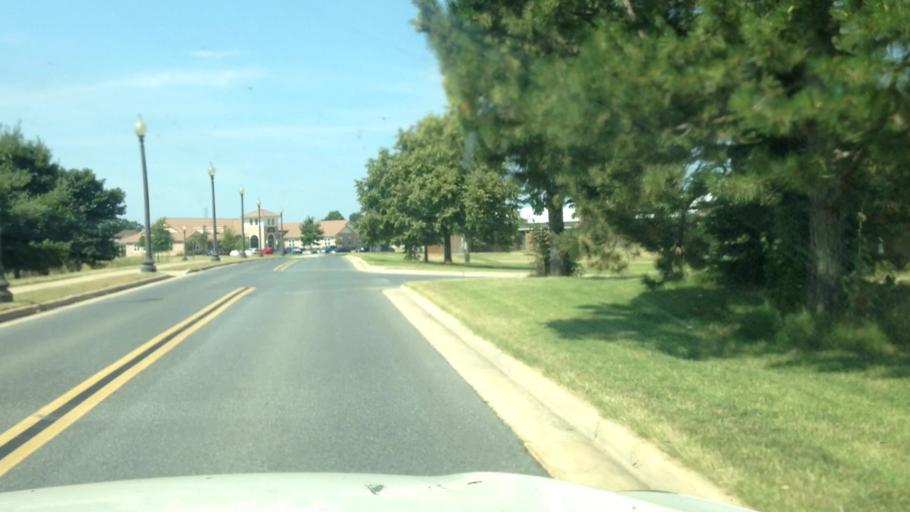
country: US
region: Maryland
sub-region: Prince George's County
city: Glassmanor
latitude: 38.8359
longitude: -77.0174
